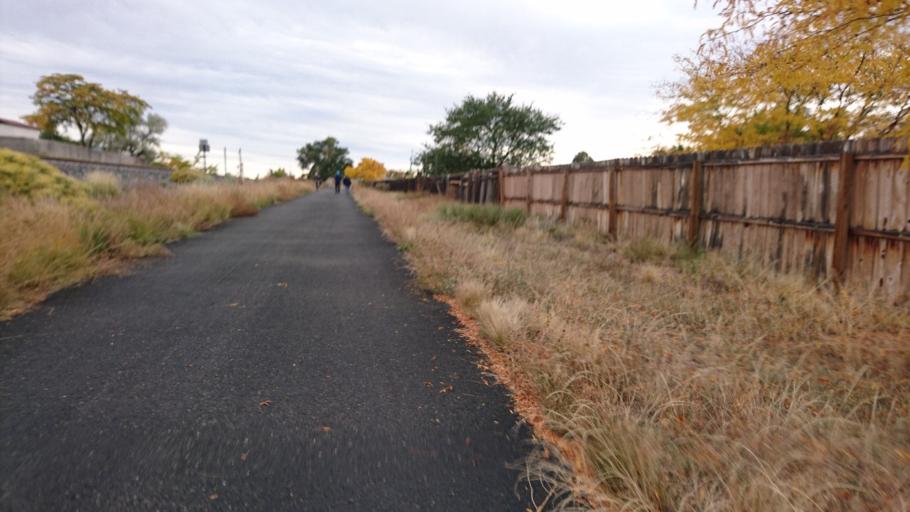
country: US
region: New Mexico
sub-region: Santa Fe County
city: Santa Fe
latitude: 35.6538
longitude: -105.9652
